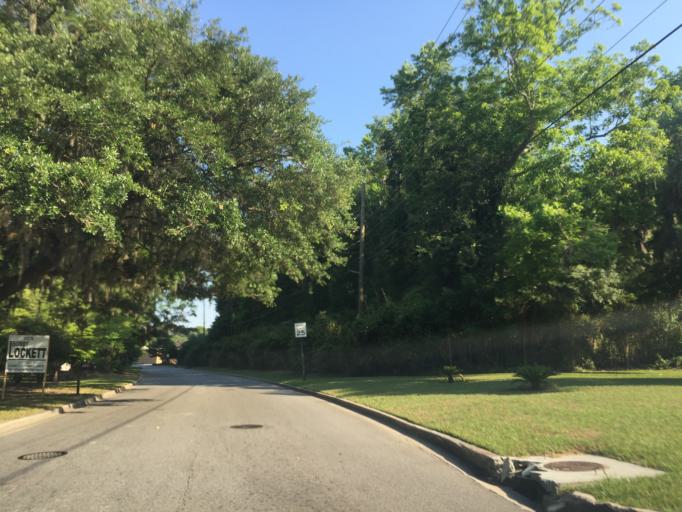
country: US
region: Georgia
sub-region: Chatham County
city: Isle of Hope
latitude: 31.9898
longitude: -81.0758
